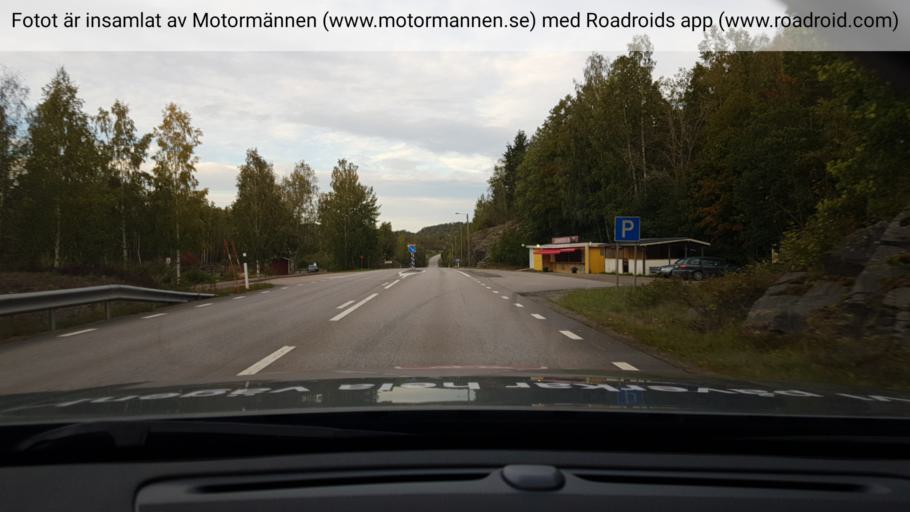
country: SE
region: Vaestra Goetaland
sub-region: Bengtsfors Kommun
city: Bengtsfors
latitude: 59.0226
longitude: 12.2753
